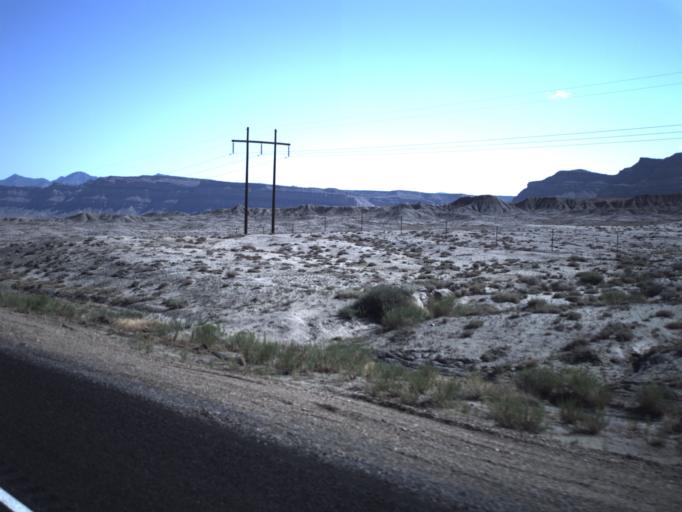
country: US
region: Utah
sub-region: Carbon County
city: East Carbon City
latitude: 39.2016
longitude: -110.3385
